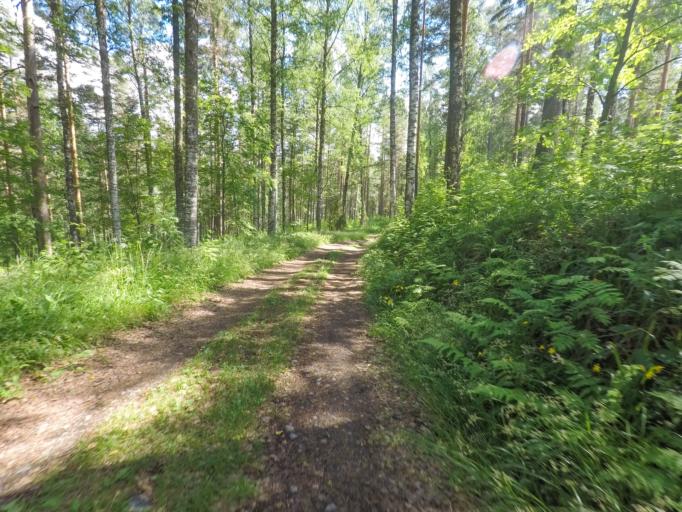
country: FI
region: Southern Savonia
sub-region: Savonlinna
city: Punkaharju
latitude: 61.8001
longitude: 29.3087
